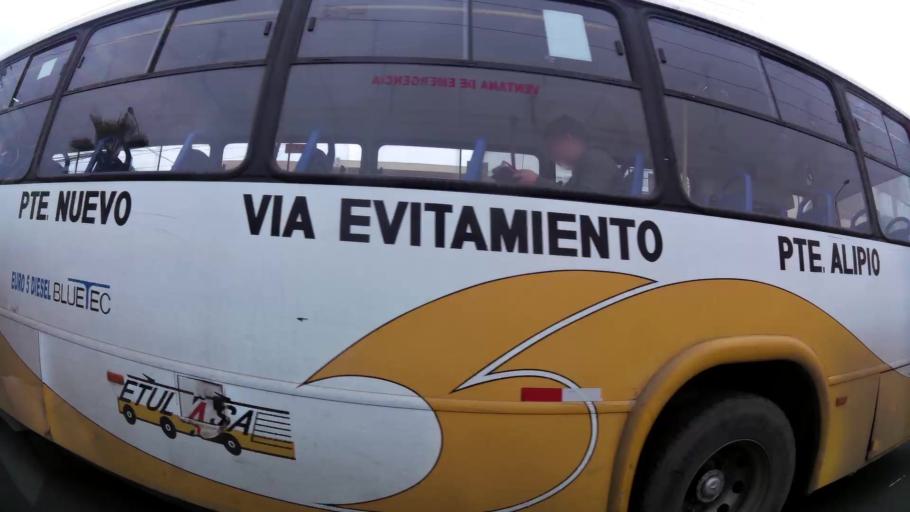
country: PE
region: Lima
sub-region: Lima
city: Surco
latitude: -12.2058
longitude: -77.0176
